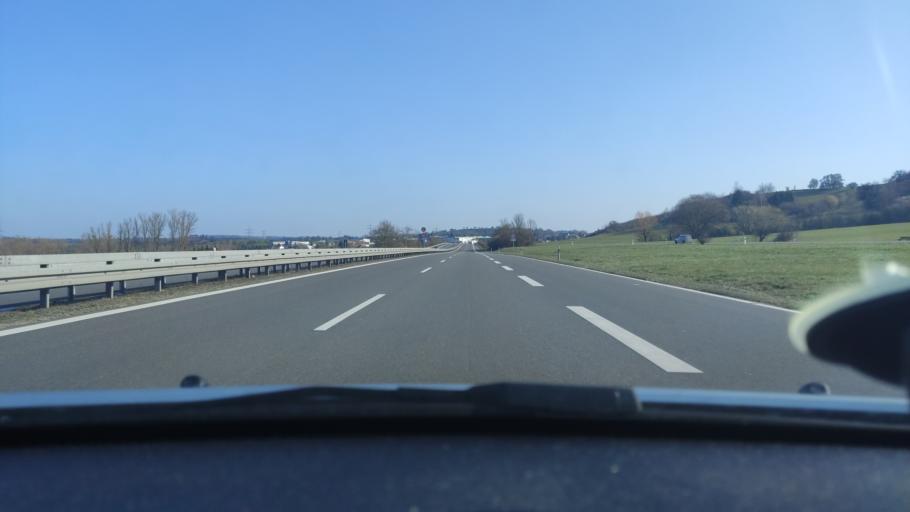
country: DE
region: Baden-Wuerttemberg
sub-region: Tuebingen Region
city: Balingen
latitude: 48.2870
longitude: 8.8624
